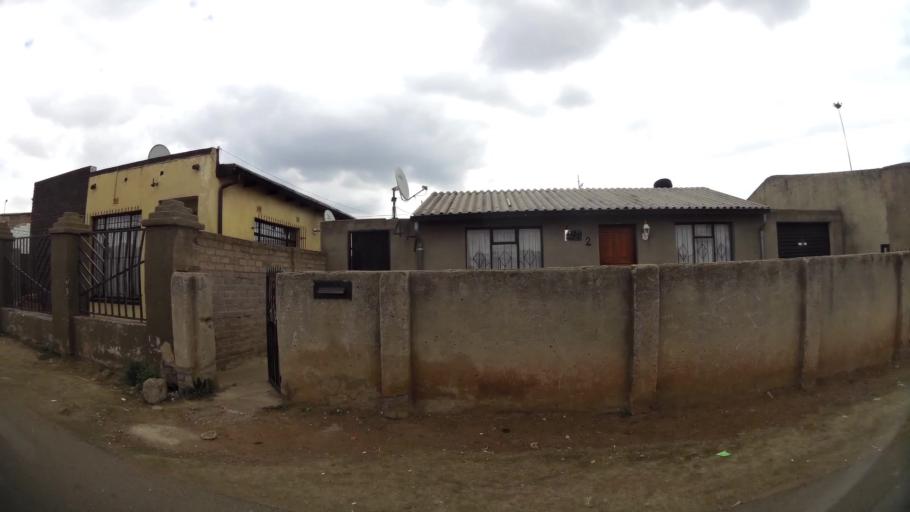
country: ZA
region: Gauteng
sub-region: City of Johannesburg Metropolitan Municipality
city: Soweto
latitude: -26.2711
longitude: 27.8704
